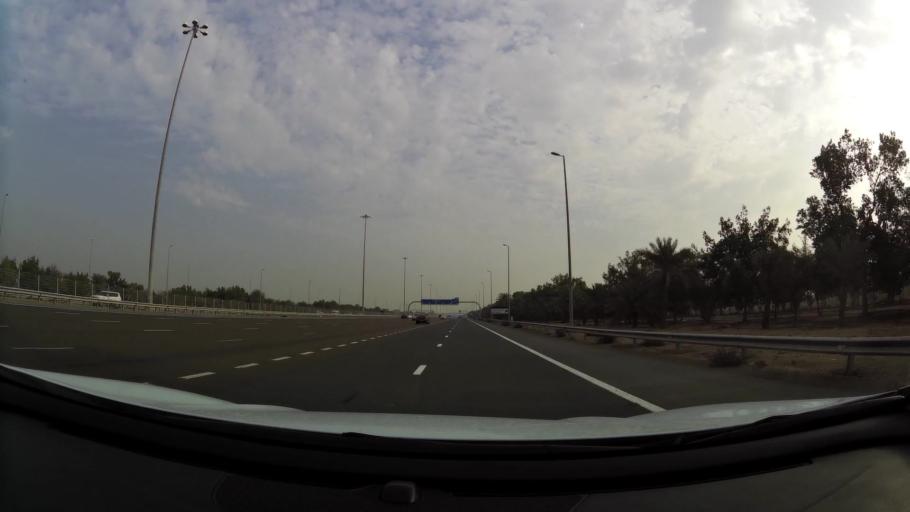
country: AE
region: Abu Dhabi
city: Abu Dhabi
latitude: 24.5007
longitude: 54.6564
